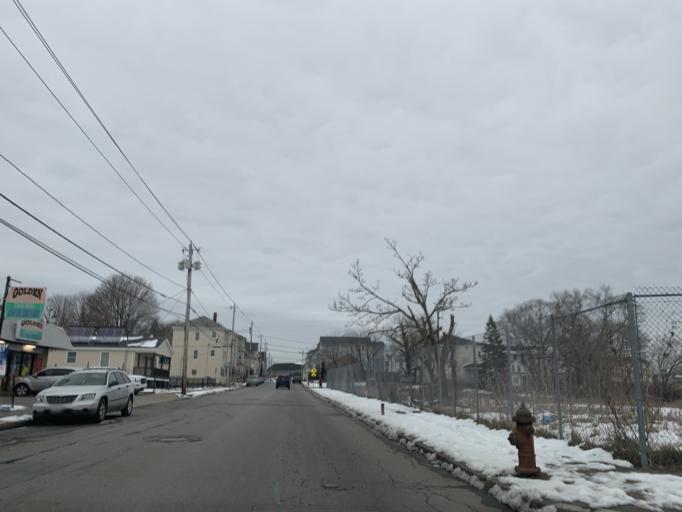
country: US
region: Massachusetts
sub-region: Bristol County
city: Fall River
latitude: 41.6878
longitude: -71.1482
